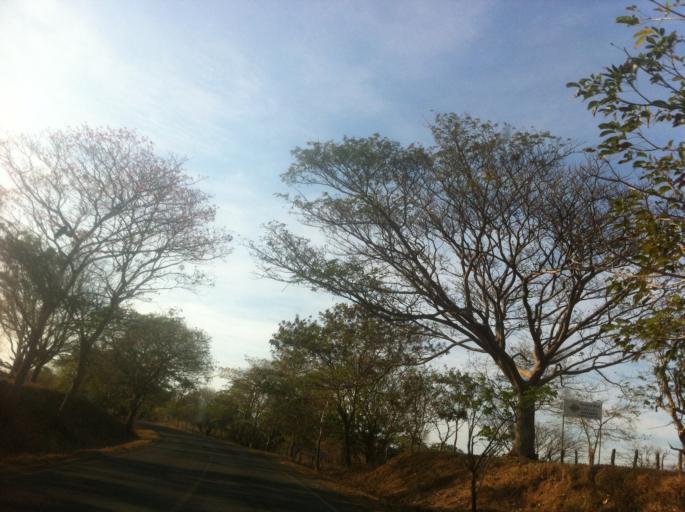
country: NI
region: Rivas
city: San Juan del Sur
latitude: 11.2976
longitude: -85.6877
